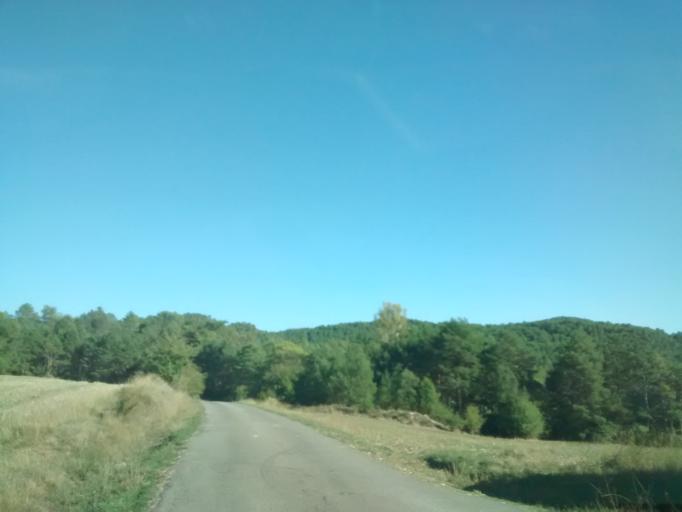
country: ES
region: Aragon
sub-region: Provincia de Huesca
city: Santa Cruz de la Seros
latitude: 42.4343
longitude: -0.6522
